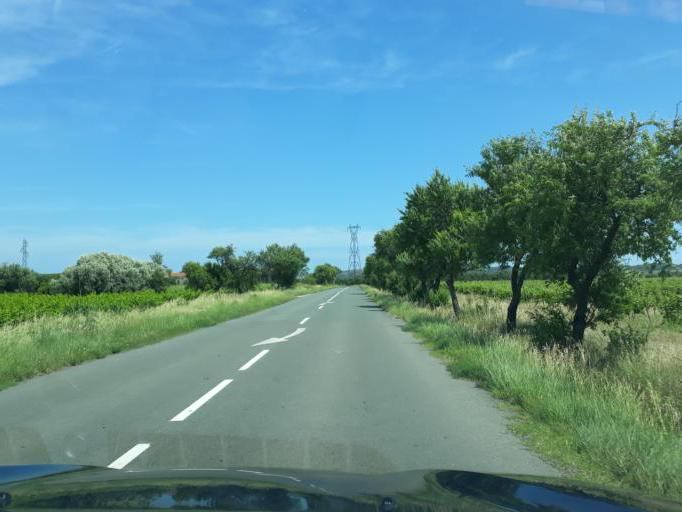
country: FR
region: Languedoc-Roussillon
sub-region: Departement de l'Aude
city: Portel-des-Corbieres
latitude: 43.0411
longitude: 2.9382
